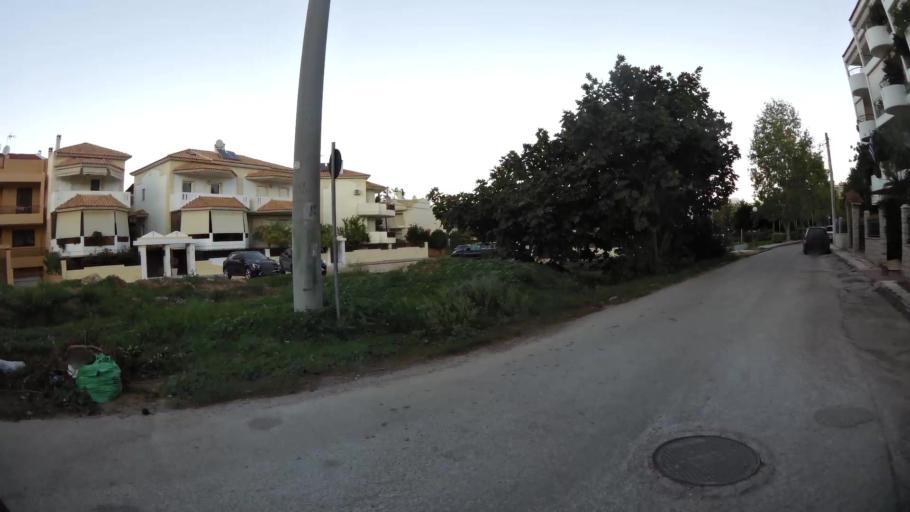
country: GR
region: Attica
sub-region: Nomarchia Anatolikis Attikis
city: Vari
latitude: 37.8215
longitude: 23.7955
